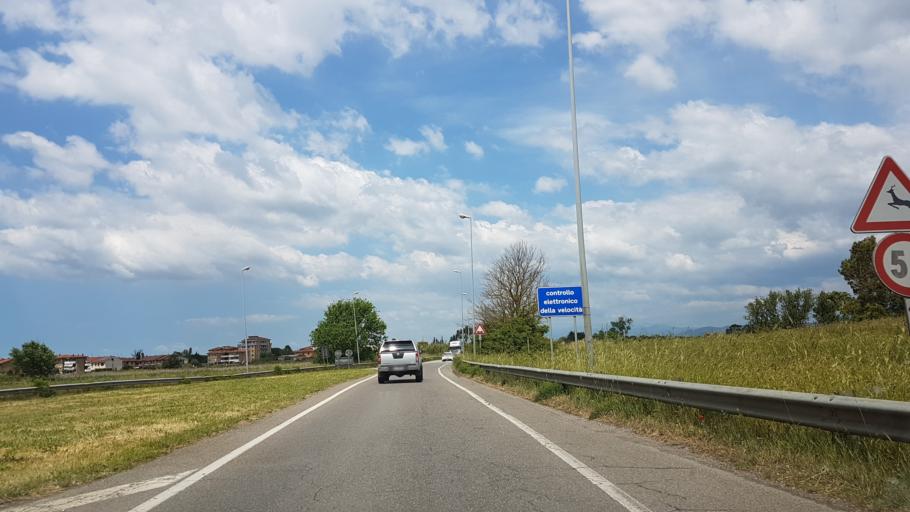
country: IT
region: Tuscany
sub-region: Provincia di Livorno
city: Vicarello
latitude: 43.6105
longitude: 10.4730
